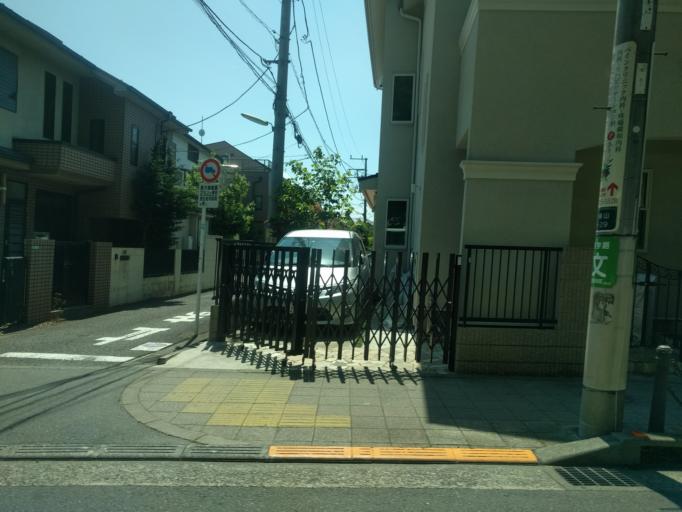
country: JP
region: Tokyo
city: Mitaka-shi
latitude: 35.6676
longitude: 139.6176
